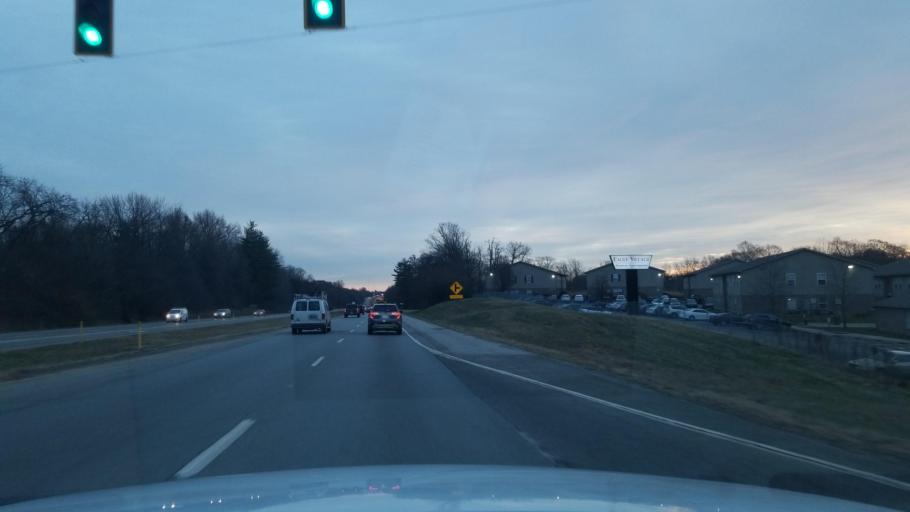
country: US
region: Indiana
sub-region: Vanderburgh County
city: Evansville
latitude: 37.9698
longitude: -87.6638
